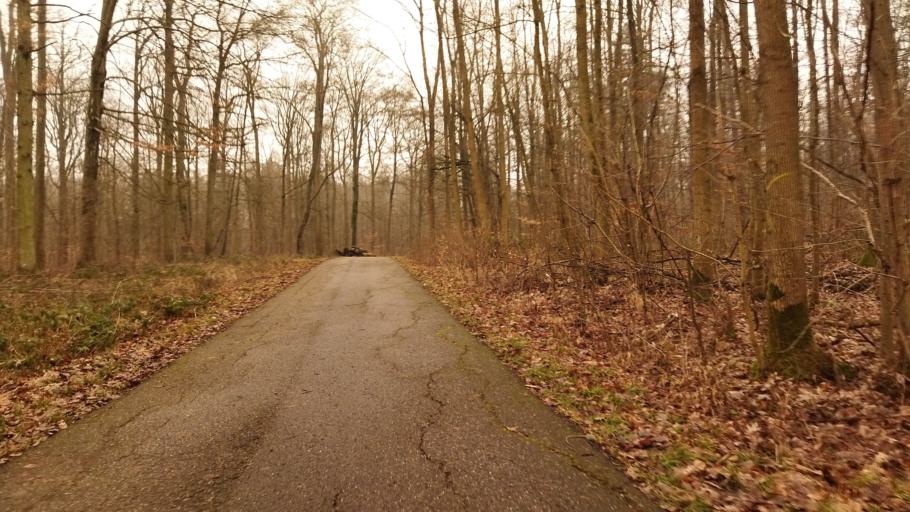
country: DE
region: Baden-Wuerttemberg
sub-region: Regierungsbezirk Stuttgart
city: Weinsberg
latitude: 49.1376
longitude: 9.2767
